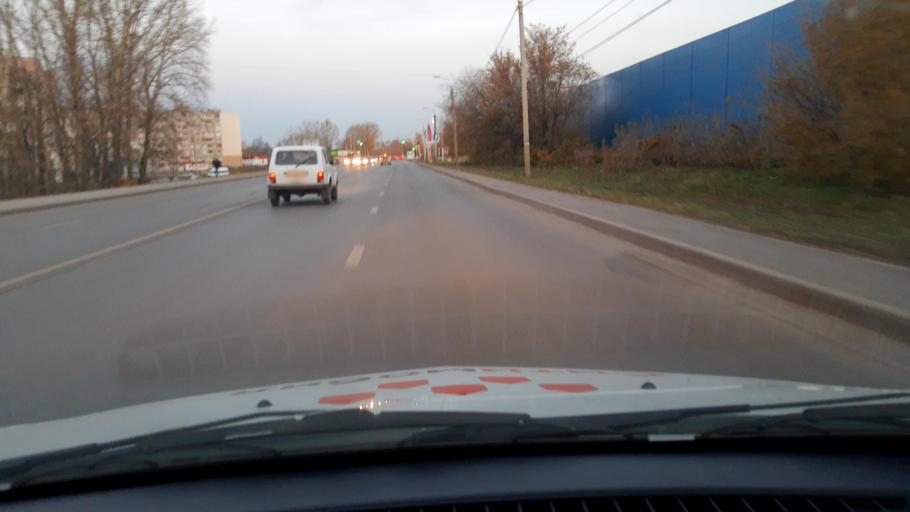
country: RU
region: Bashkortostan
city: Iglino
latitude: 54.7683
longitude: 56.2344
